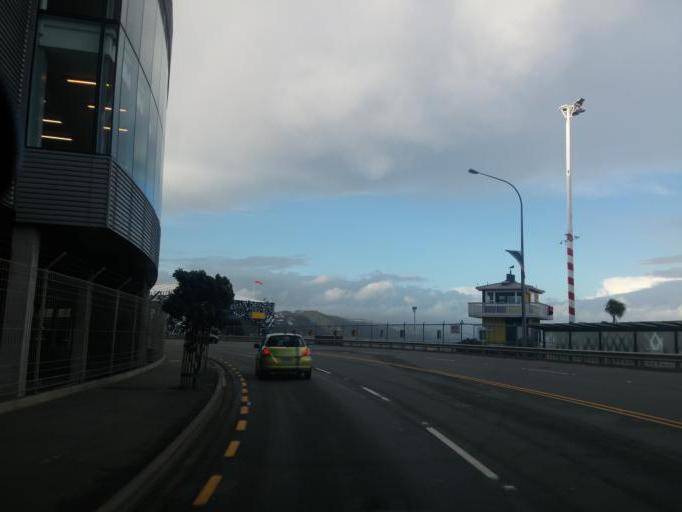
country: NZ
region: Wellington
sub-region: Wellington City
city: Wellington
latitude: -41.2735
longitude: 174.7869
